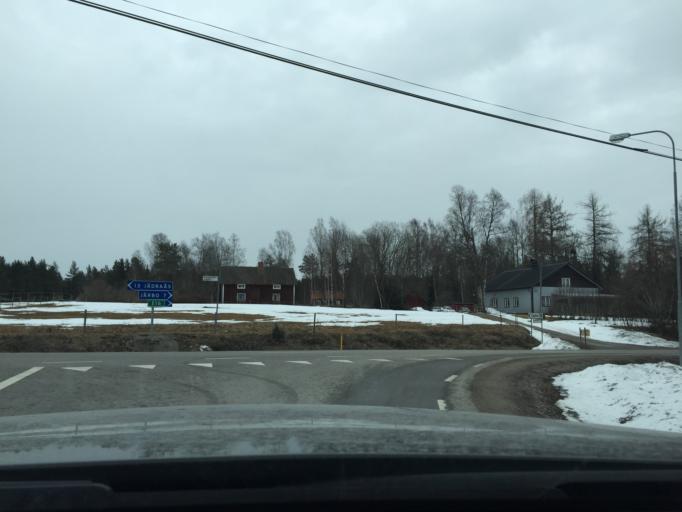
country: SE
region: Gaevleborg
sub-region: Sandvikens Kommun
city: Jarbo
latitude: 60.7594
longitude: 16.5352
